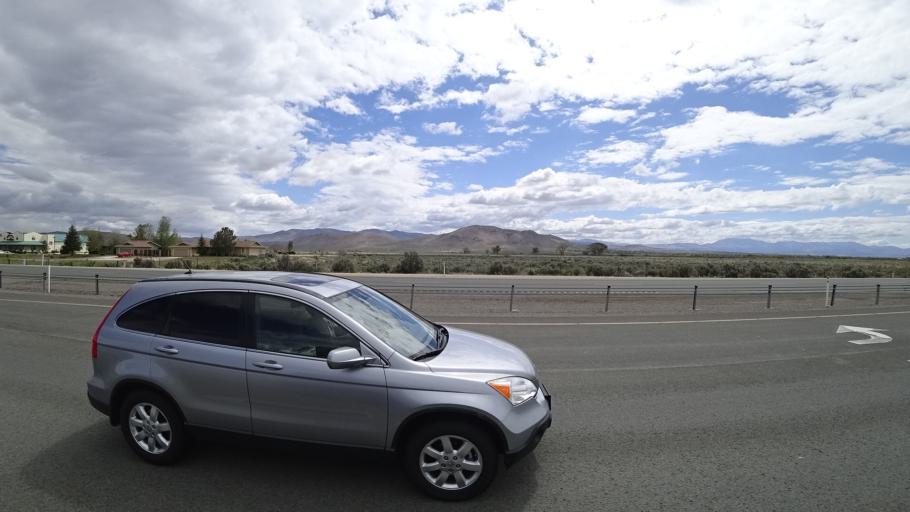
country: US
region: Nevada
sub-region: Douglas County
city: Indian Hills
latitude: 39.0675
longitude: -119.7802
